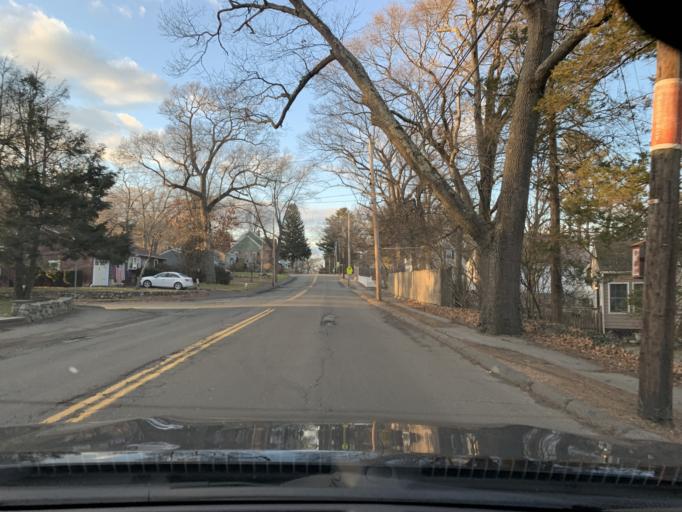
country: US
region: Massachusetts
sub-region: Essex County
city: Lynnfield
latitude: 42.5222
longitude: -71.0191
